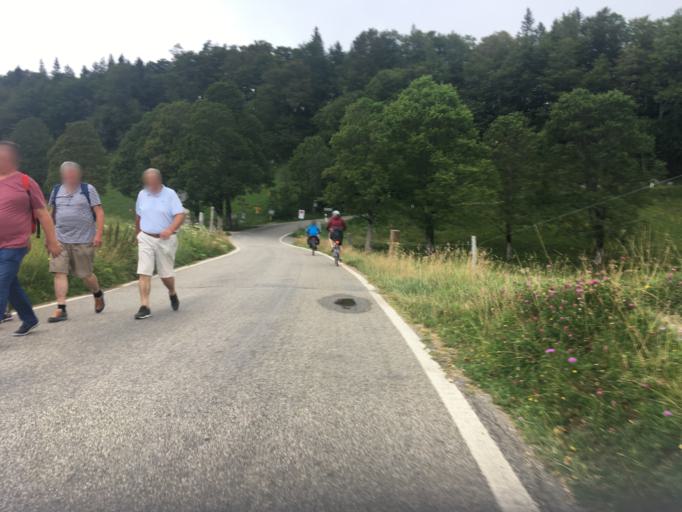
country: CH
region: Solothurn
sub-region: Bezirk Thal
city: Welschenrohr
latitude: 47.2537
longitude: 7.5074
